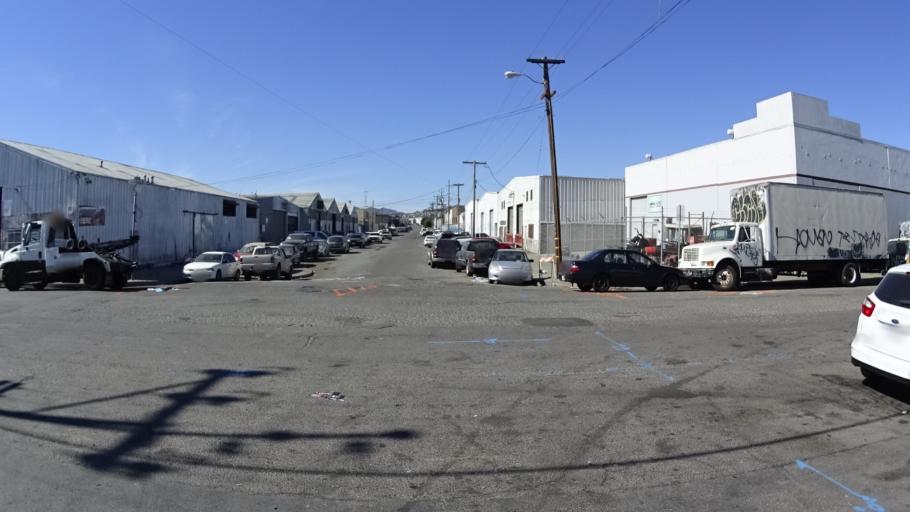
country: US
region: California
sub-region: San Mateo County
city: Brisbane
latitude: 37.7253
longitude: -122.3873
